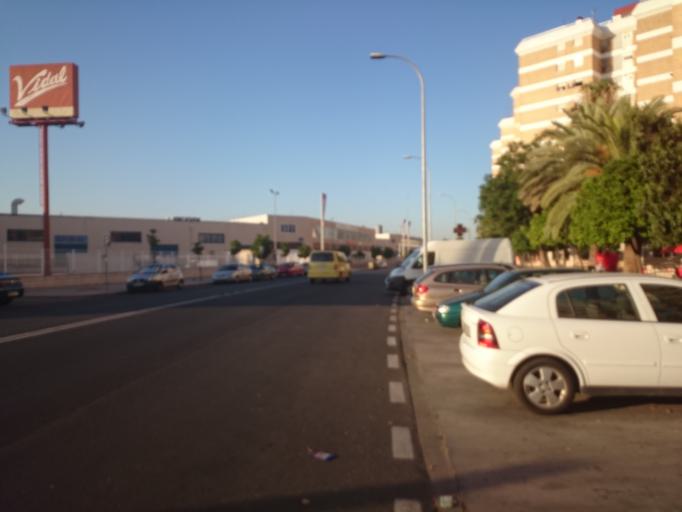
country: ES
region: Andalusia
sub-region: Provincia de Sevilla
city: Sevilla
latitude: 37.3941
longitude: -5.9576
